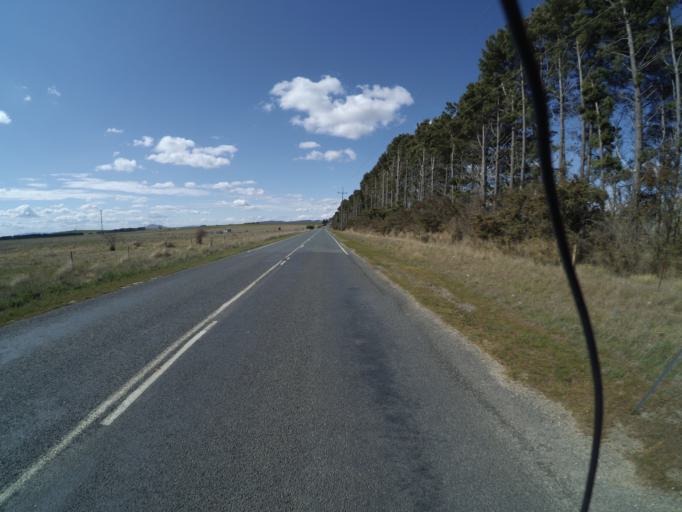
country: AU
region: New South Wales
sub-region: Palerang
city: Bungendore
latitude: -35.2270
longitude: 149.4521
